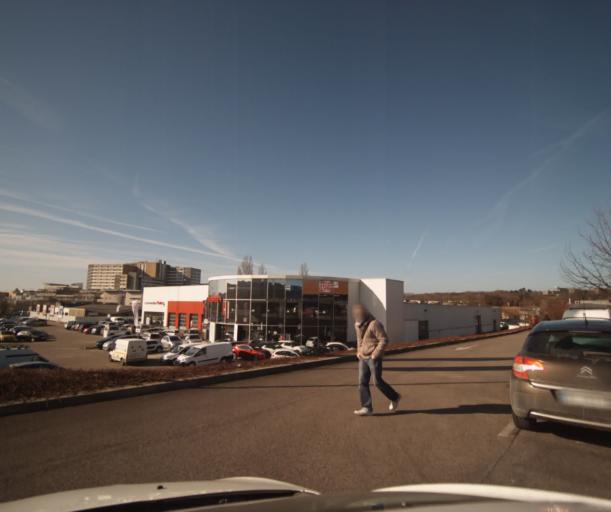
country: FR
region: Franche-Comte
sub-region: Departement du Doubs
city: Avanne-Aveney
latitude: 47.2243
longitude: 5.9686
